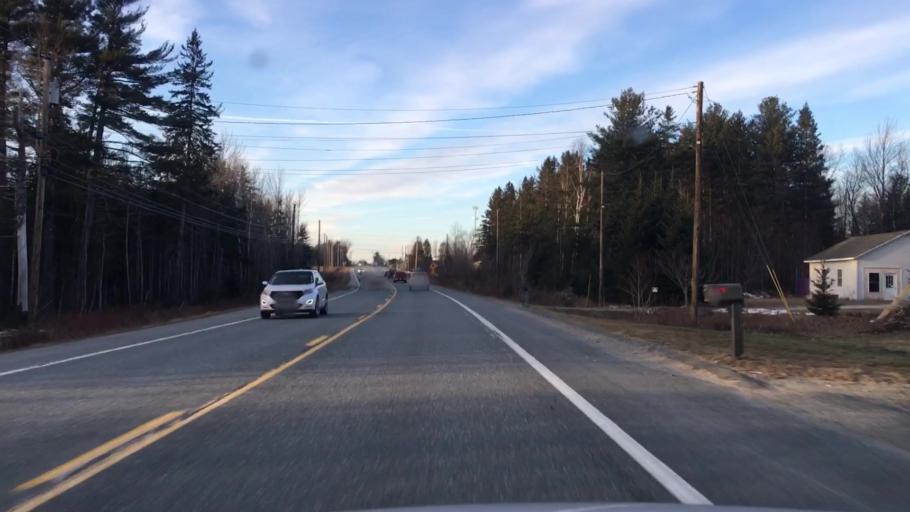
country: US
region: Maine
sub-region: Hancock County
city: Surry
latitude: 44.6124
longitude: -68.5220
